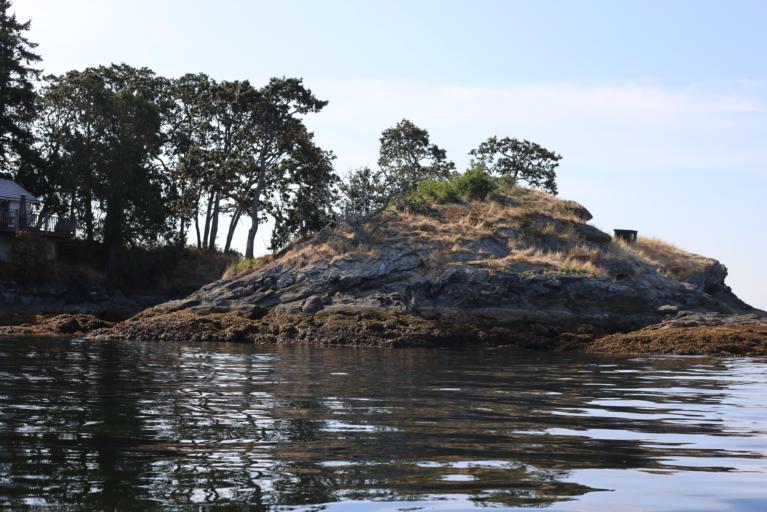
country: CA
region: British Columbia
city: North Saanich
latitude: 48.6777
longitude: -123.4893
